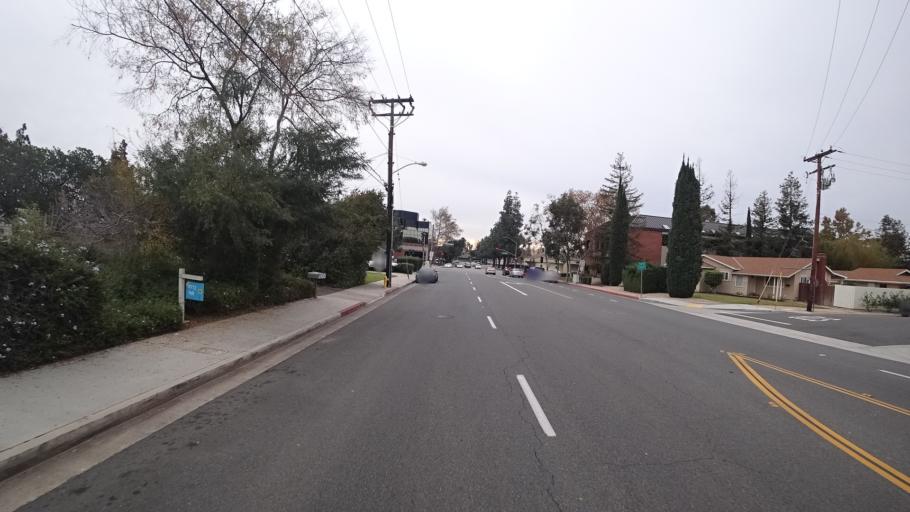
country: US
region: California
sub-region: Orange County
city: Tustin
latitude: 33.7492
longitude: -117.8143
